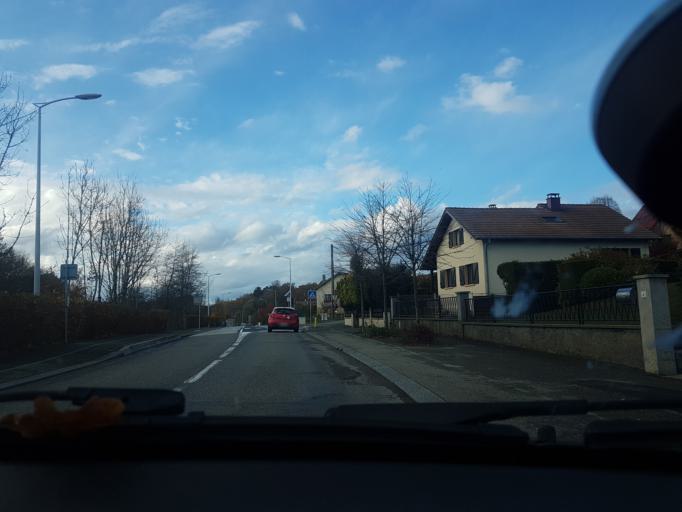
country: FR
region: Franche-Comte
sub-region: Territoire de Belfort
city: Essert
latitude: 47.6384
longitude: 6.8034
